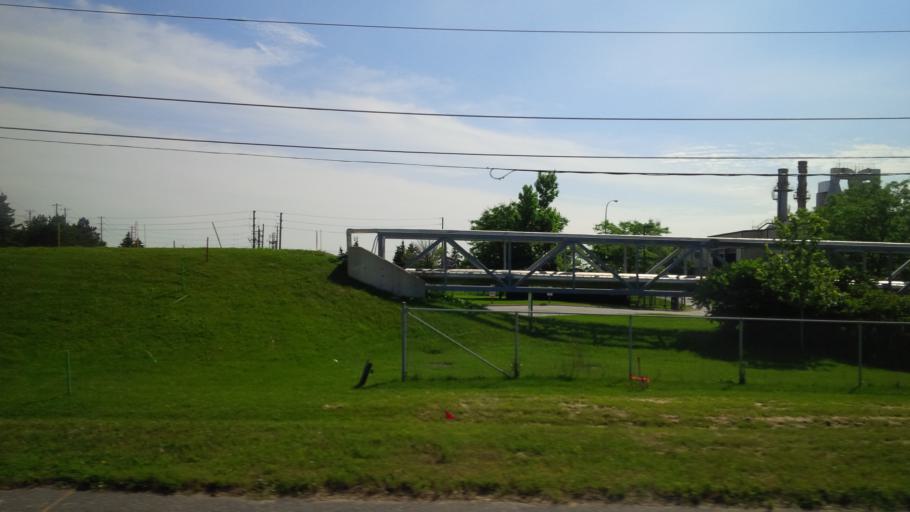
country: CA
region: Ontario
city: Brampton
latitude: 43.6974
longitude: -79.6806
